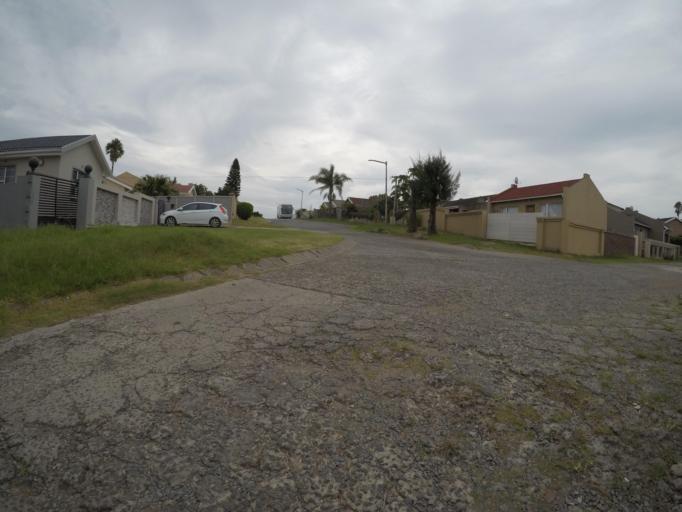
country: ZA
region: Eastern Cape
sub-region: Buffalo City Metropolitan Municipality
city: East London
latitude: -32.9936
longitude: 27.8630
